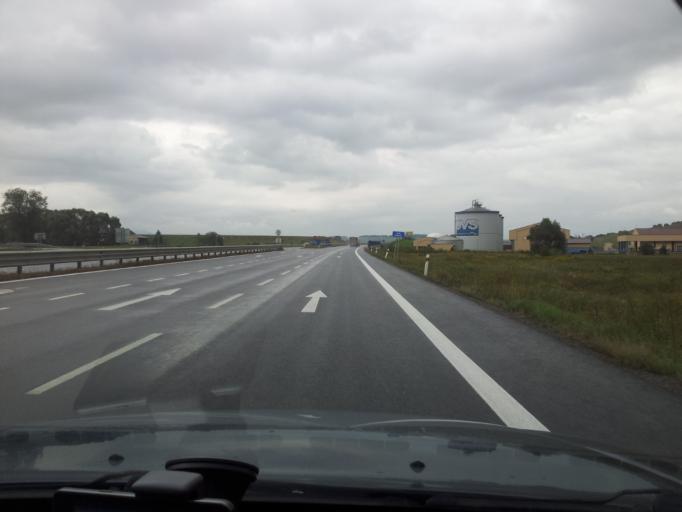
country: SK
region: Presovsky
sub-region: Okres Poprad
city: Poprad
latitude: 49.0930
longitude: 20.3389
